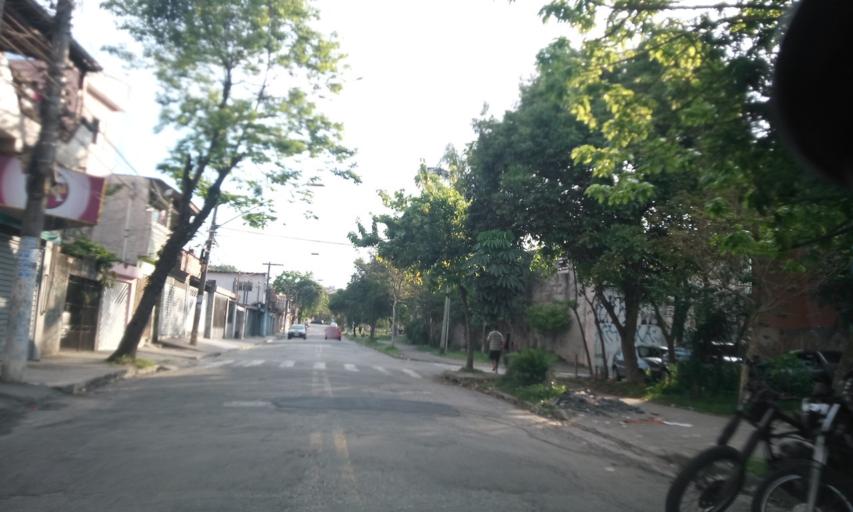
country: BR
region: Sao Paulo
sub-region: Santo Andre
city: Santo Andre
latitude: -23.7052
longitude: -46.5075
